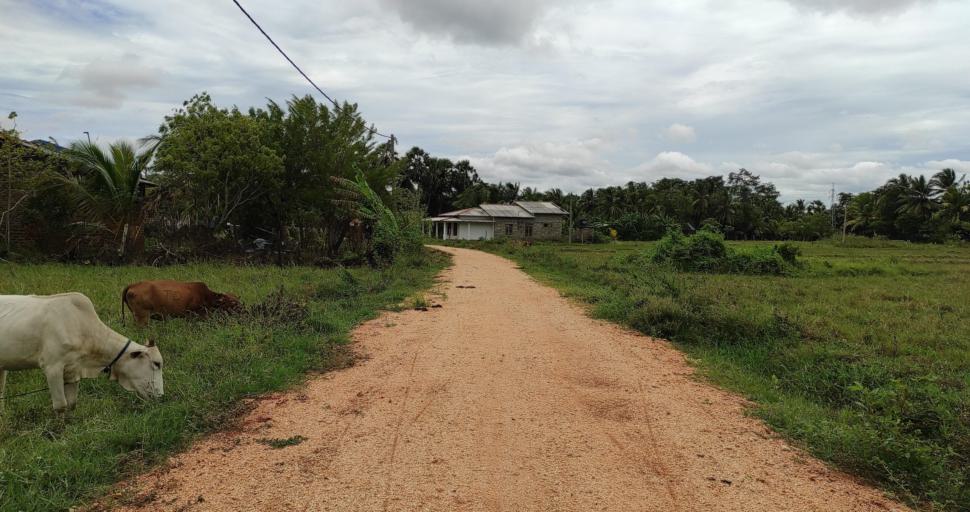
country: LK
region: Eastern Province
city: Trincomalee
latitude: 8.4454
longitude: 81.0523
